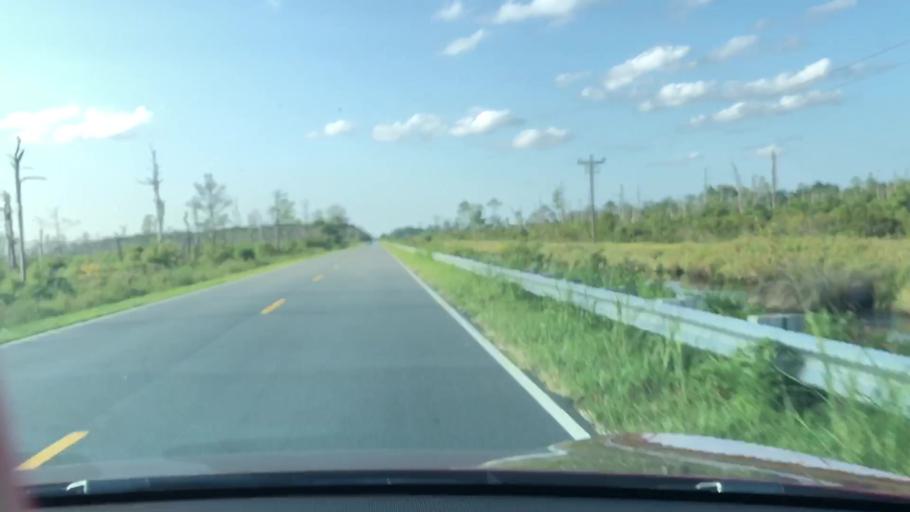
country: US
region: North Carolina
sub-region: Dare County
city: Wanchese
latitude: 35.6605
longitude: -75.7773
